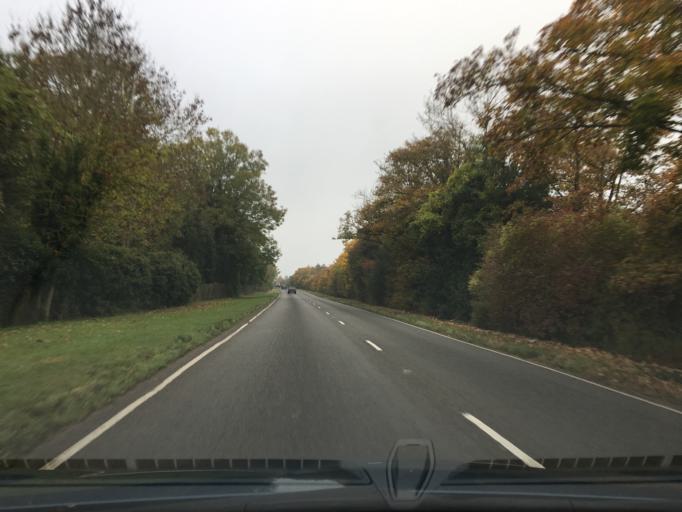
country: GB
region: England
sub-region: Surrey
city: Normandy
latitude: 51.2268
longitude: -0.6866
